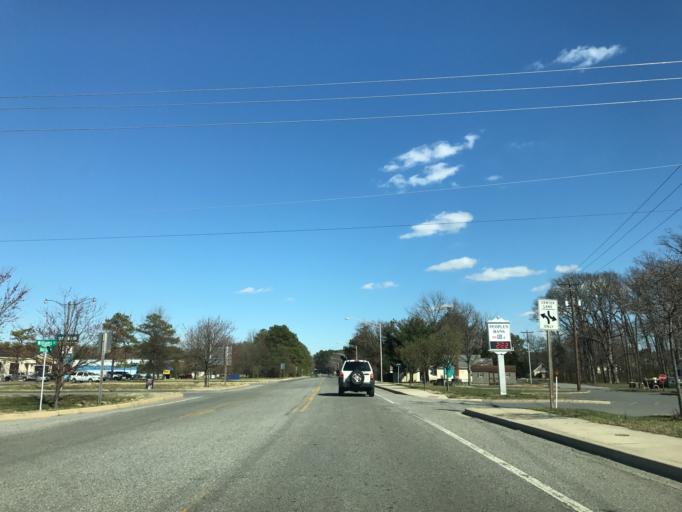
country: US
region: Maryland
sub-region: Kent County
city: Rock Hall
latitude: 39.1385
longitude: -76.2340
